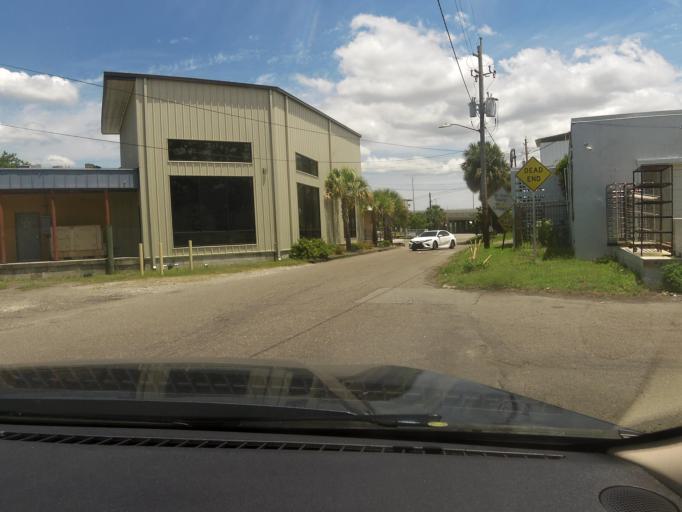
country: US
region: Florida
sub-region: Duval County
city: Jacksonville
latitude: 30.3911
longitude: -81.6482
